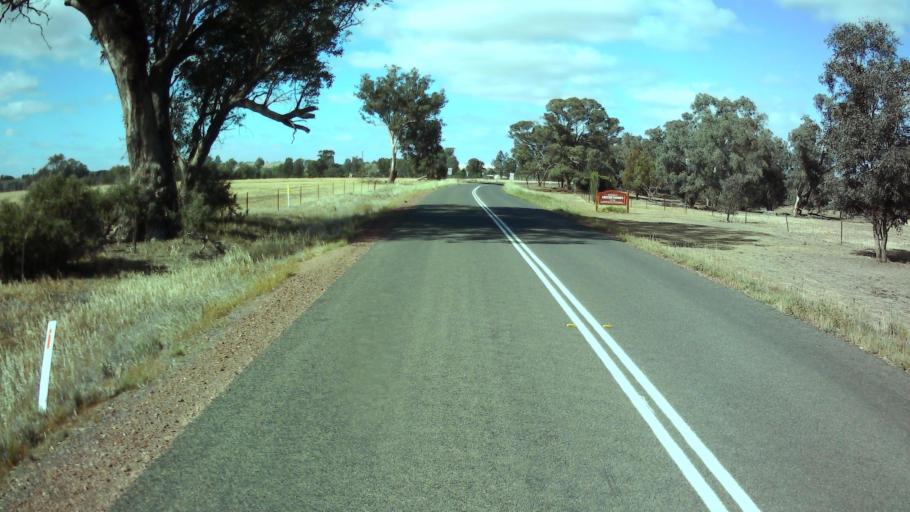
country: AU
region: New South Wales
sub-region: Weddin
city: Grenfell
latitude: -33.9907
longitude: 148.4087
